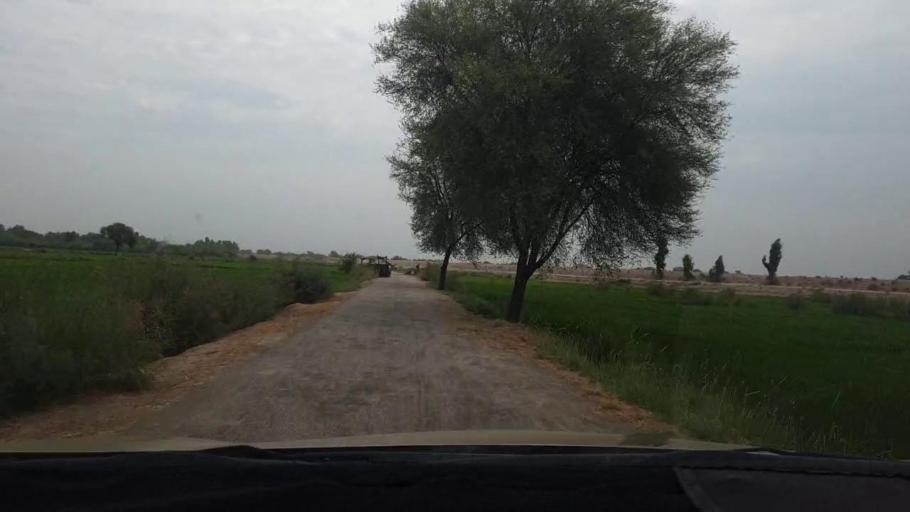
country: PK
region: Sindh
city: Naudero
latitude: 27.6213
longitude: 68.3308
